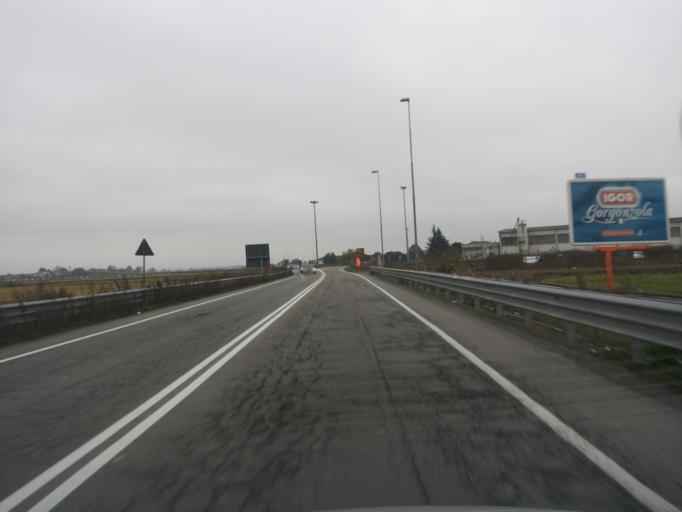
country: IT
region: Piedmont
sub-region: Provincia di Novara
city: Lumellogno
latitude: 45.4206
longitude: 8.5719
